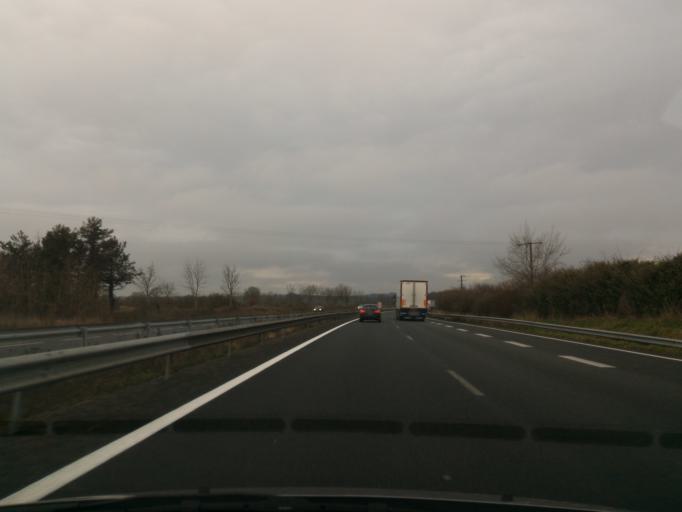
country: FR
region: Poitou-Charentes
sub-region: Departement de la Vienne
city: Fontaine-le-Comte
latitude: 46.5019
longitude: 0.2778
